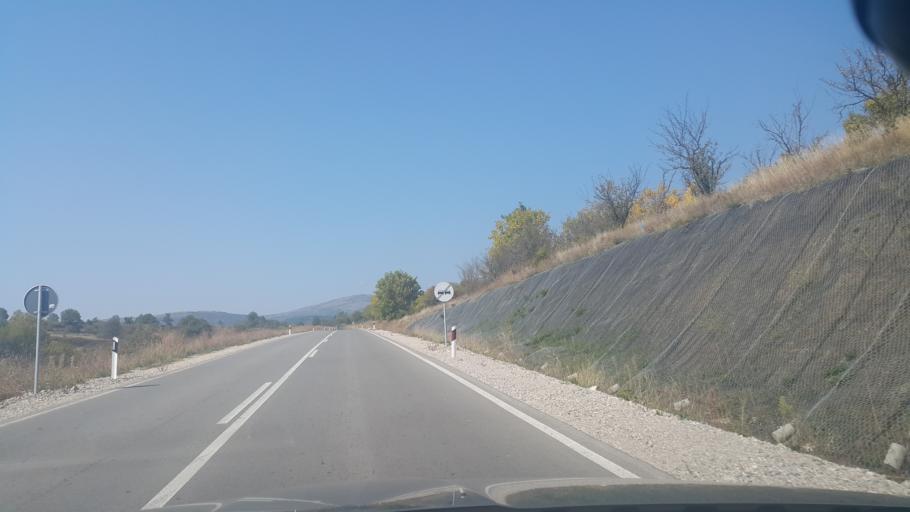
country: RS
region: Central Serbia
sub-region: Pirotski Okrug
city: Bela Palanka
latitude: 43.2314
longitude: 22.4237
